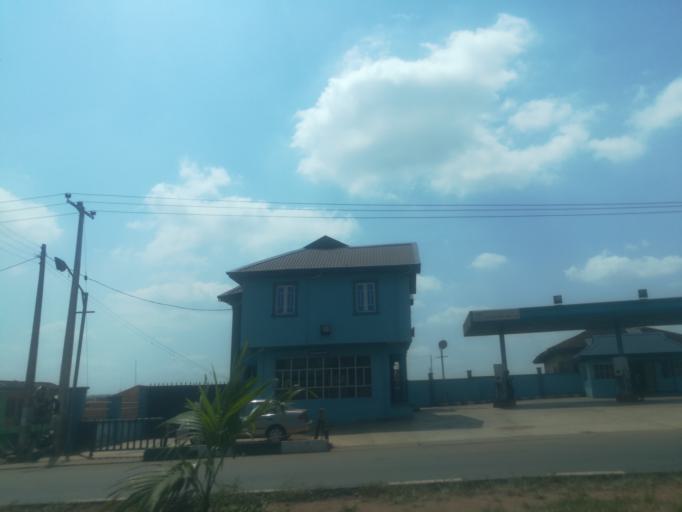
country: NG
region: Ogun
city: Abeokuta
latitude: 7.1511
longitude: 3.3533
